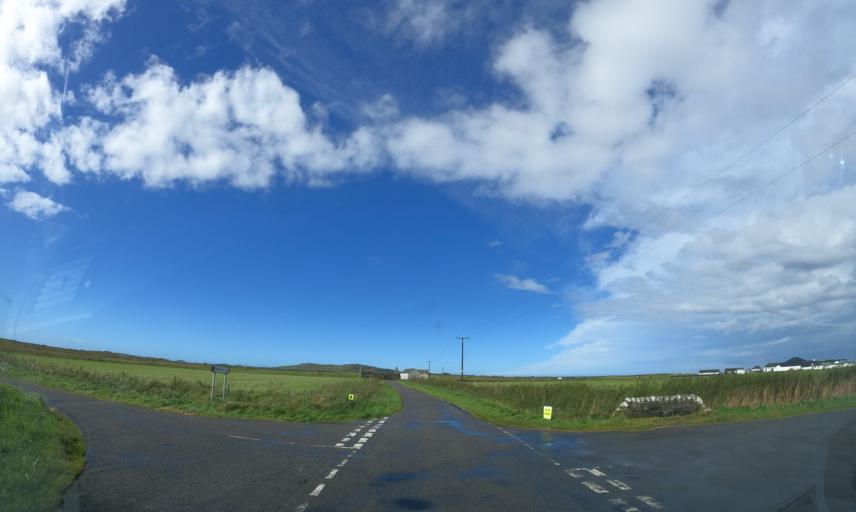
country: GB
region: Scotland
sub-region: Eilean Siar
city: Barra
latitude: 56.5204
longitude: -6.9128
